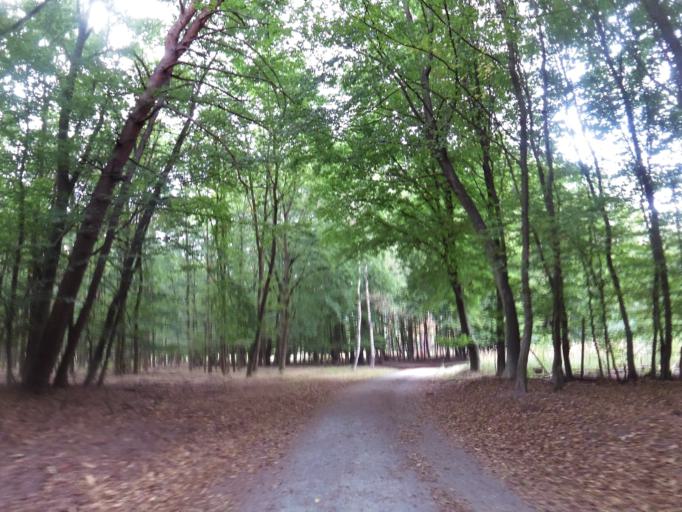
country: DE
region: Hesse
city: Morfelden-Walldorf
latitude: 50.0130
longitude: 8.5527
